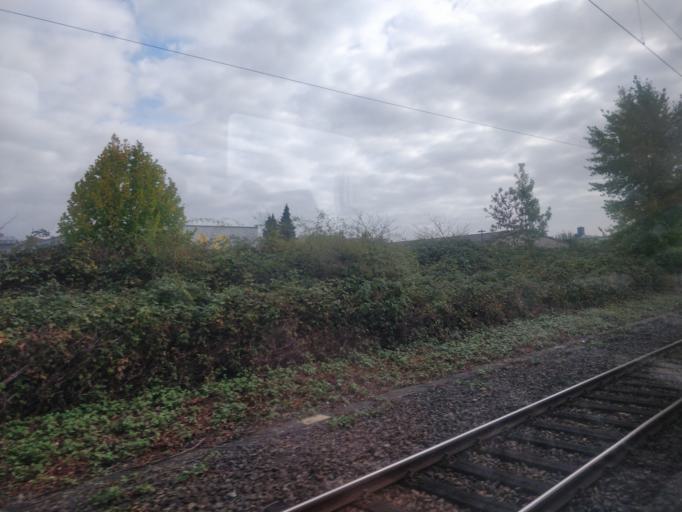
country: DE
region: North Rhine-Westphalia
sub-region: Regierungsbezirk Koln
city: Siegburg
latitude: 50.8005
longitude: 7.1929
